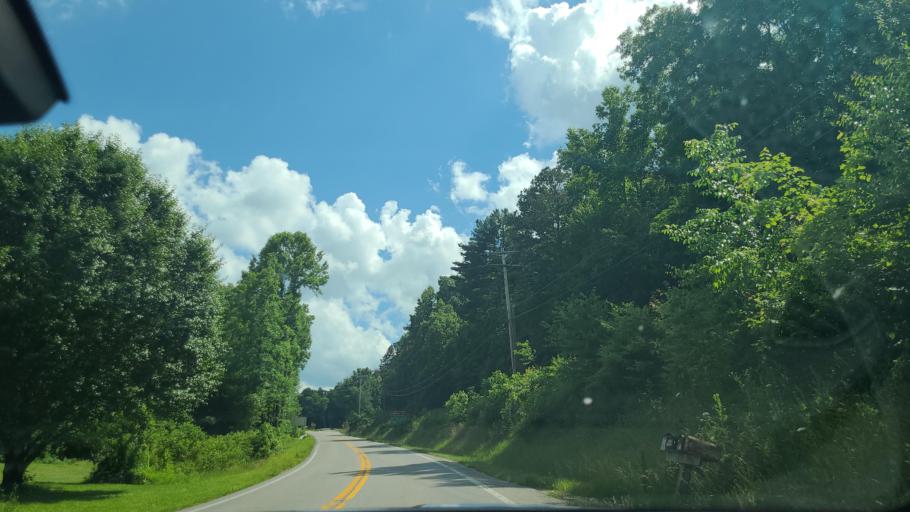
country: US
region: Kentucky
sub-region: Whitley County
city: Williamsburg
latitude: 36.8588
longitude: -84.2323
